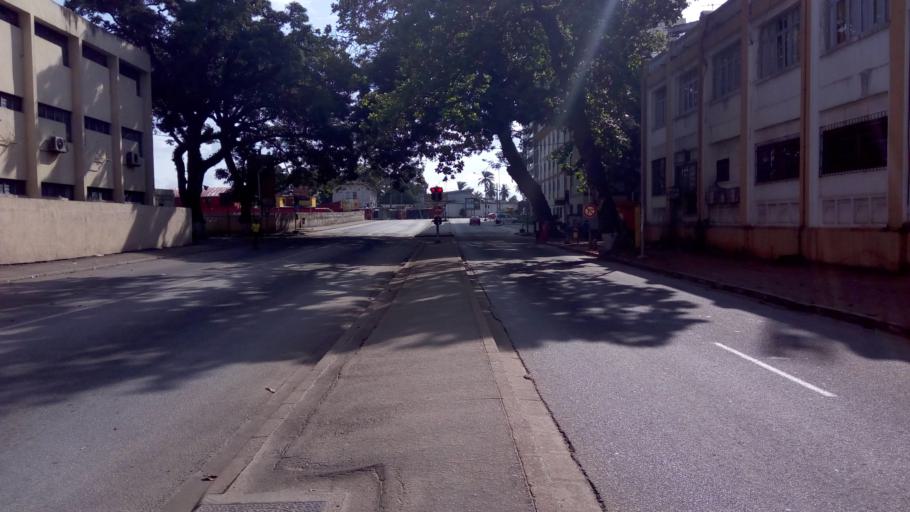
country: CI
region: Lagunes
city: Abidjan
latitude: 5.3253
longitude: -4.0212
